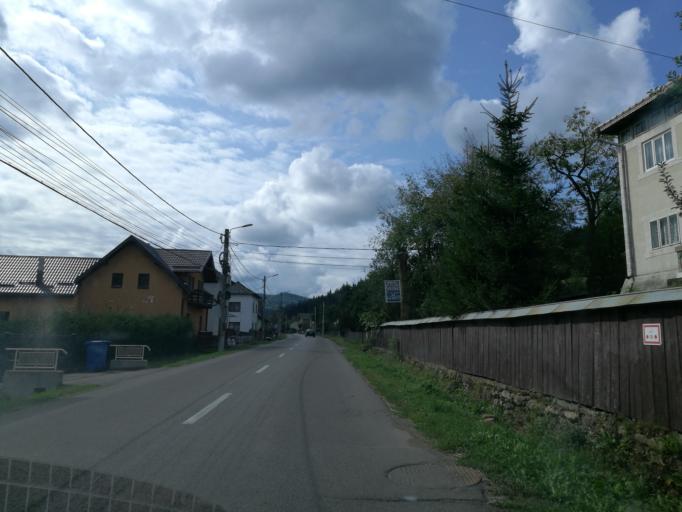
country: RO
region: Suceava
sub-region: Oras Gura Humorului
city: Gura Humorului
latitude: 47.5343
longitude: 25.8646
